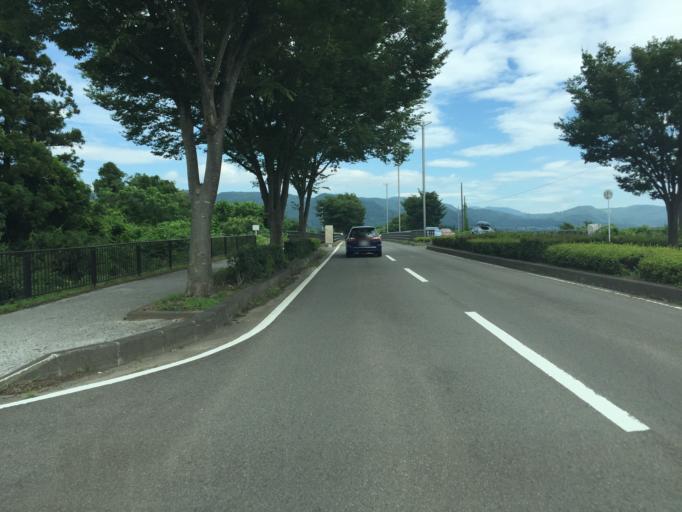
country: JP
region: Fukushima
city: Fukushima-shi
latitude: 37.7514
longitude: 140.3800
